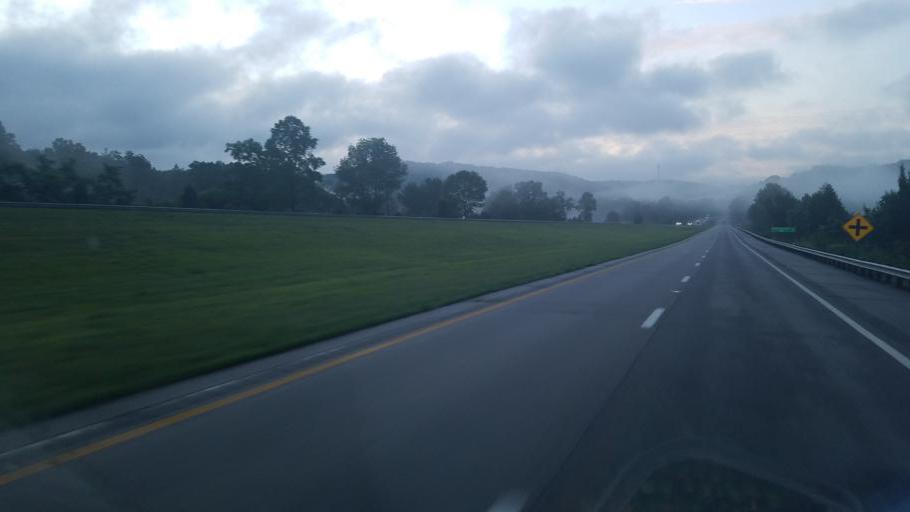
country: US
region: Ohio
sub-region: Jackson County
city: Jackson
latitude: 39.1919
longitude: -82.7782
